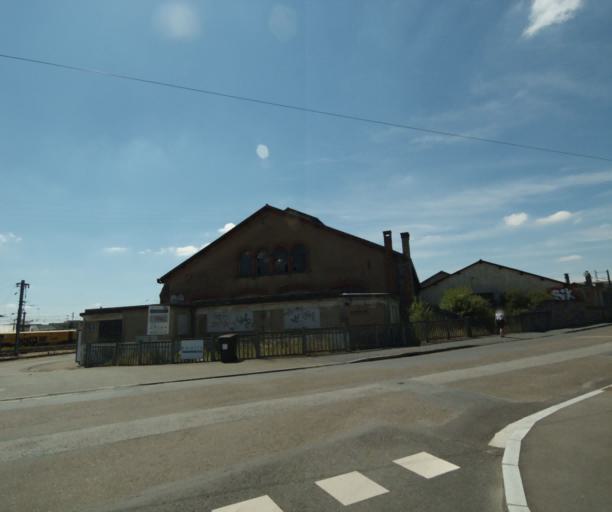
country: FR
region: Pays de la Loire
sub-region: Departement de la Mayenne
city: Laval
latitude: 48.0771
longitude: -0.7543
